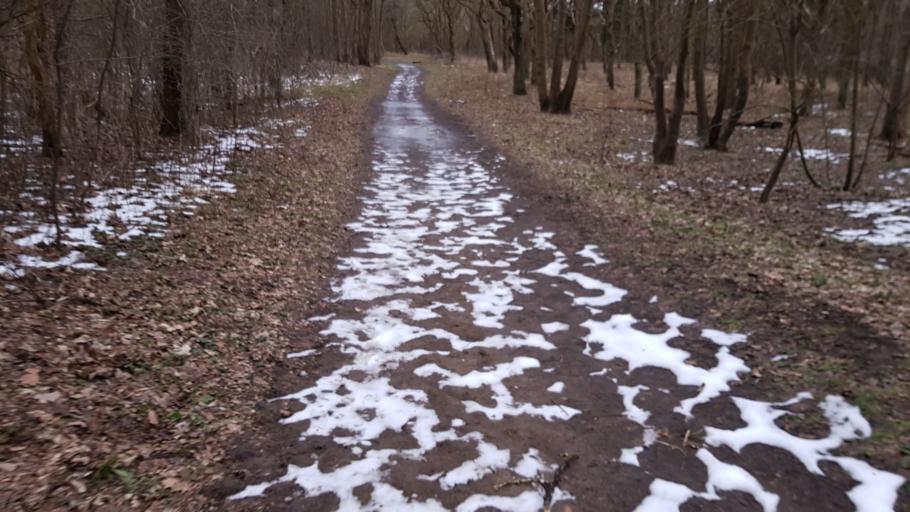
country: NL
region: North Holland
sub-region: Gemeente Bergen
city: Egmond aan Zee
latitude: 52.5992
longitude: 4.6355
